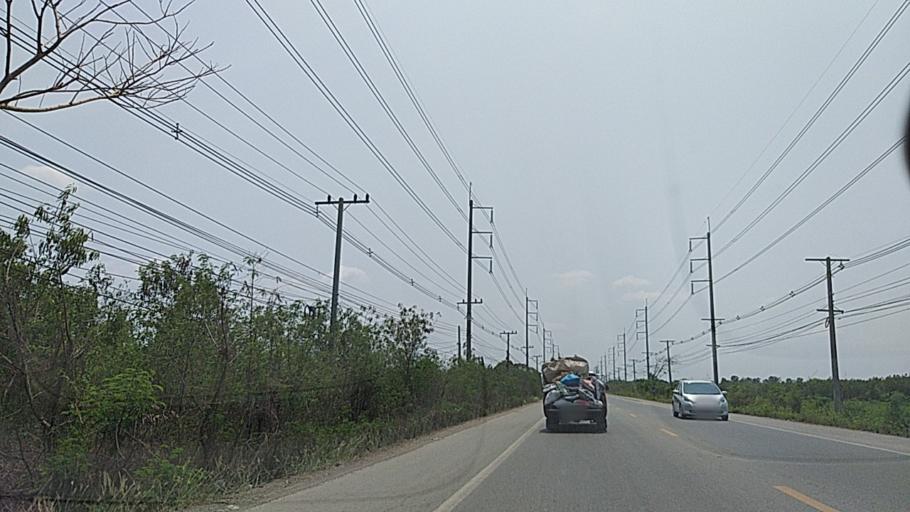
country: TH
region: Chachoengsao
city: Bang Nam Priao
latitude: 13.8095
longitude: 101.0535
